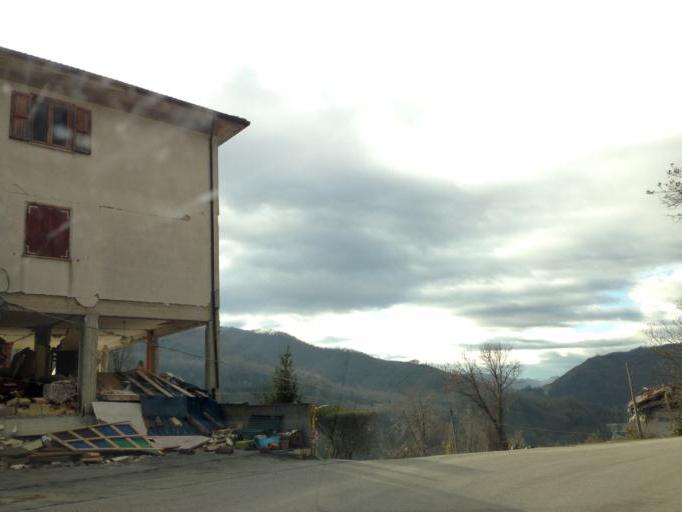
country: IT
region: The Marches
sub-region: Provincia di Ascoli Piceno
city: Arquata del Tronto
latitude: 42.7538
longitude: 13.2744
